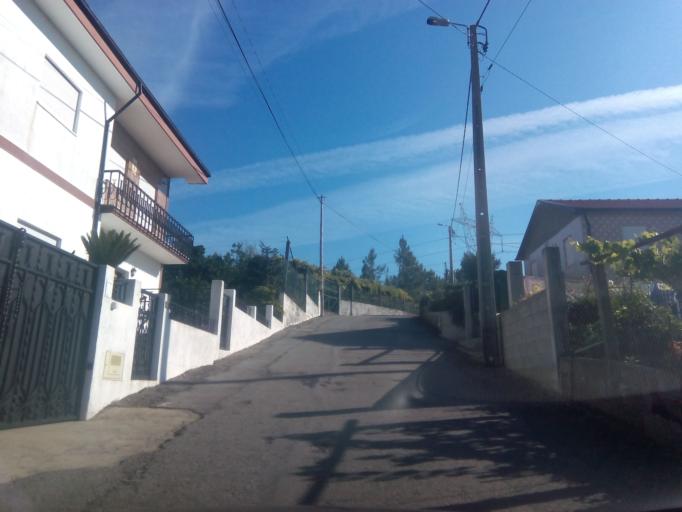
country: PT
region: Porto
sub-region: Paredes
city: Gandra
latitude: 41.2025
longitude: -8.4369
